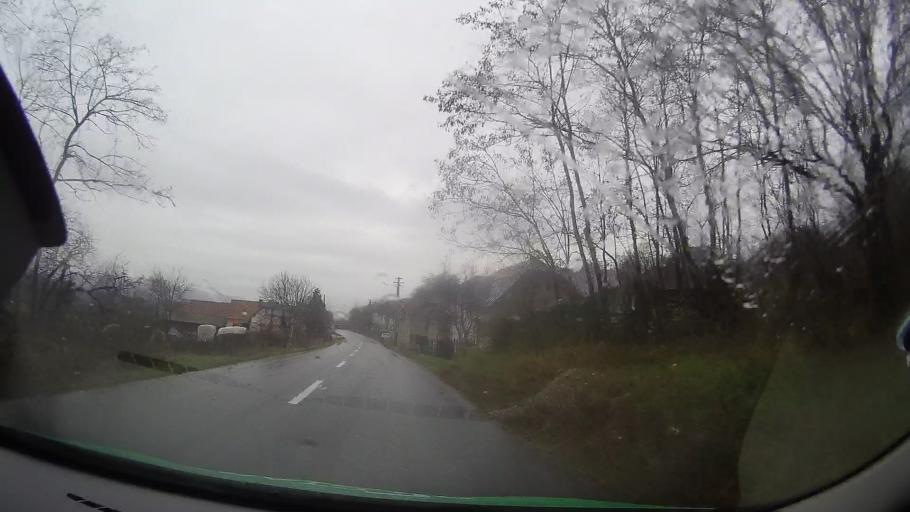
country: RO
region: Bistrita-Nasaud
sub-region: Comuna Mariselu
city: Mariselu
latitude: 47.0130
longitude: 24.5113
